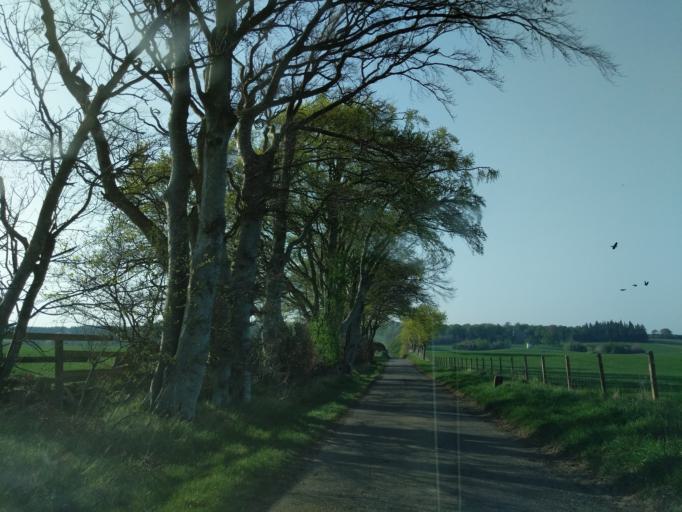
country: GB
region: Scotland
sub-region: Fife
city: Pathhead
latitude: 55.8503
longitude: -2.9183
